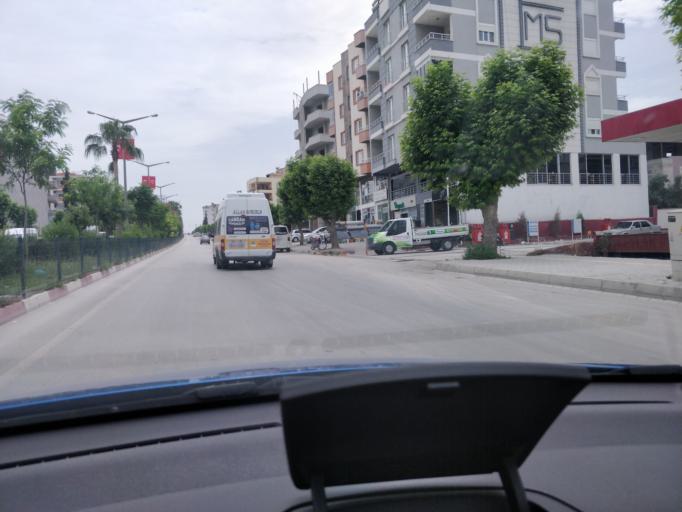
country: TR
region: Mersin
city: Mut
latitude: 36.6412
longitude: 33.4413
